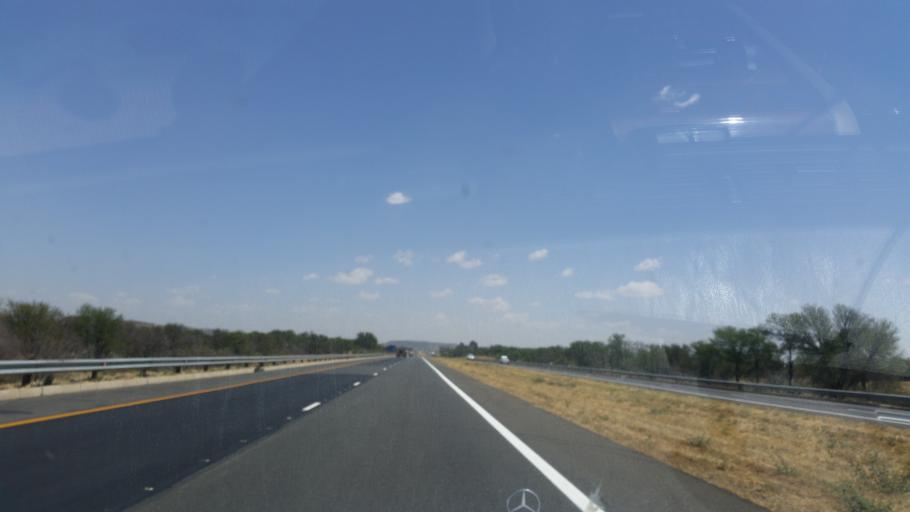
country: ZA
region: Orange Free State
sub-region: Mangaung Metropolitan Municipality
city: Bloemfontein
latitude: -28.9602
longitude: 26.3657
